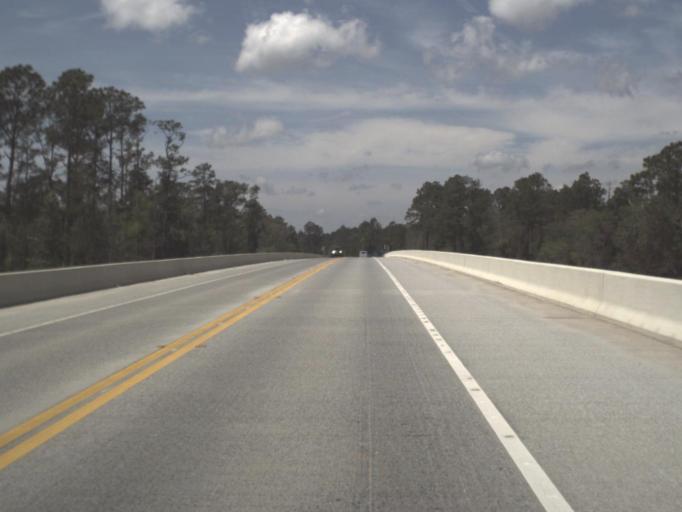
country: US
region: Florida
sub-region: Escambia County
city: Cantonment
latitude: 30.5220
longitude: -87.4457
